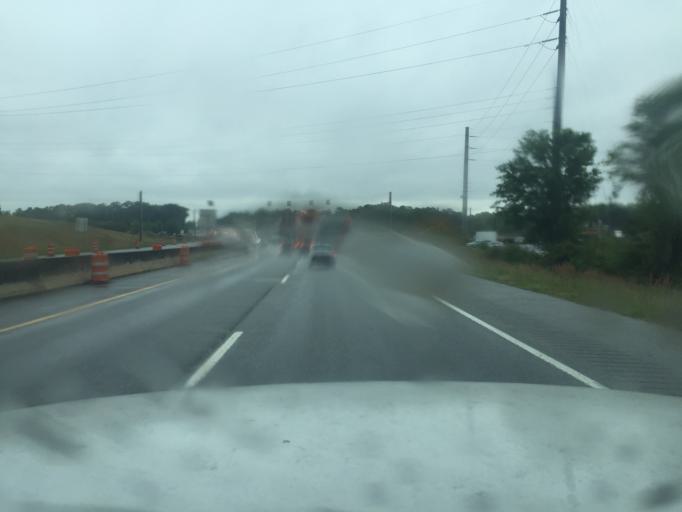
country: US
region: Georgia
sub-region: Chatham County
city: Georgetown
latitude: 31.9868
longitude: -81.2197
